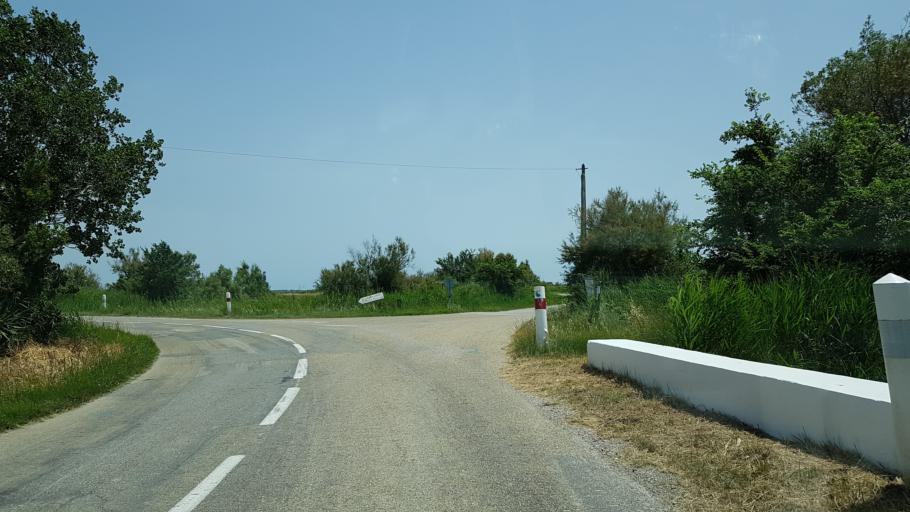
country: FR
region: Provence-Alpes-Cote d'Azur
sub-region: Departement des Bouches-du-Rhone
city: Port-Saint-Louis-du-Rhone
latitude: 43.4292
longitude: 4.6936
